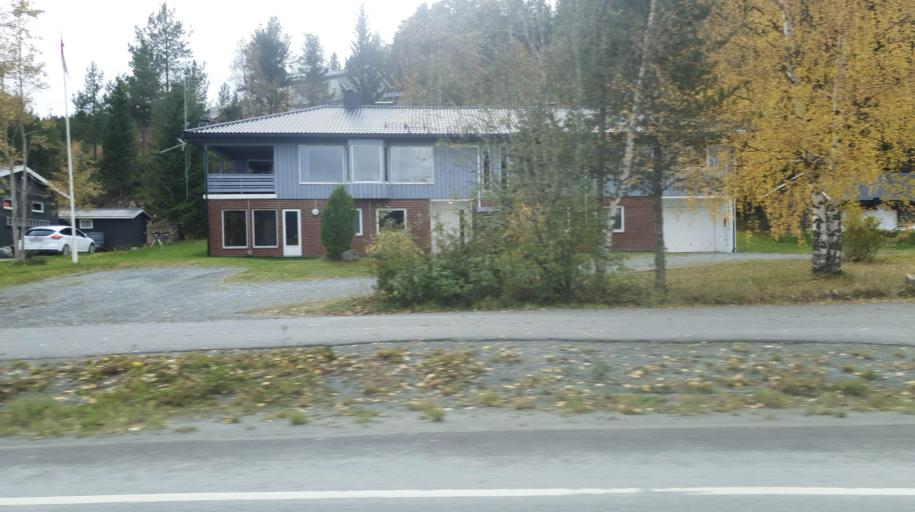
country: NO
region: Sor-Trondelag
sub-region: Klaebu
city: Klaebu
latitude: 63.3114
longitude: 10.4304
